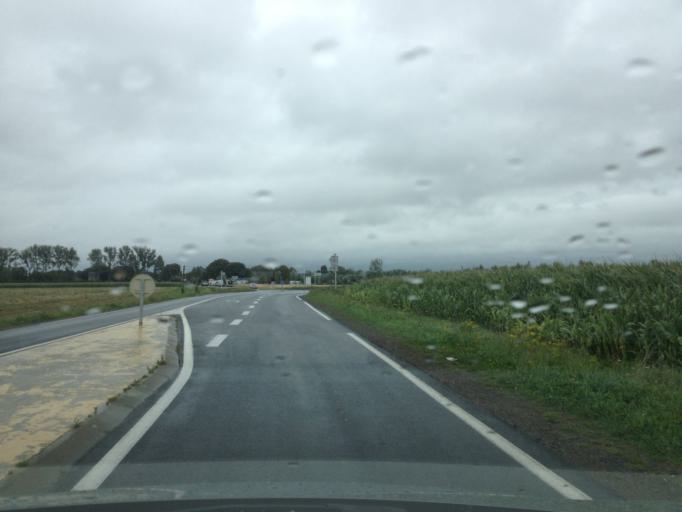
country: FR
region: Lower Normandy
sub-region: Departement de la Manche
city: Pontorson
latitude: 48.6071
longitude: -1.5106
